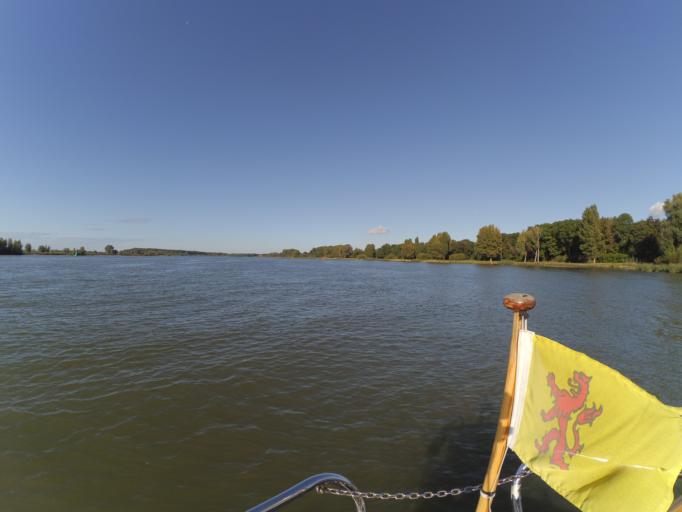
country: NL
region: South Holland
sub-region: Gemeente Zwijndrecht
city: Heerjansdam
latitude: 51.8325
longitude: 4.5465
